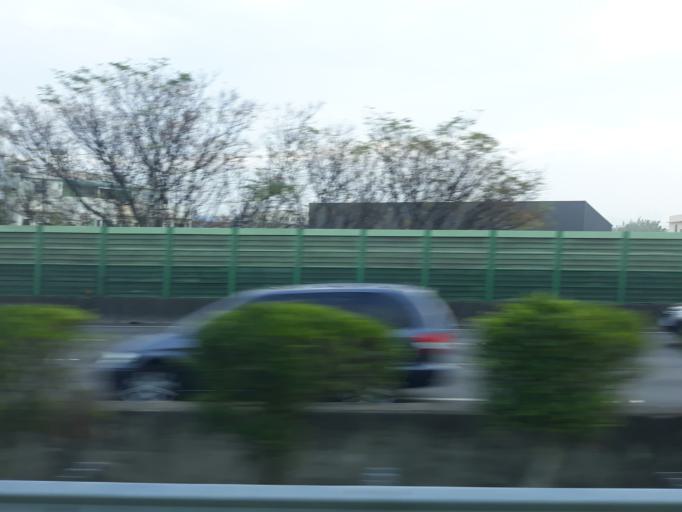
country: TW
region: Taiwan
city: Fengyuan
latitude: 24.2588
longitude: 120.6914
